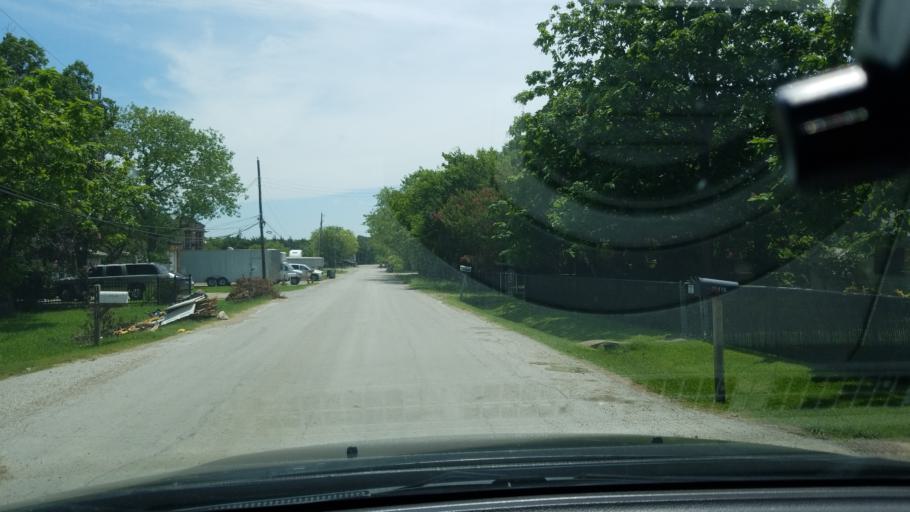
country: US
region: Texas
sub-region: Dallas County
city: Balch Springs
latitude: 32.7436
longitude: -96.6295
